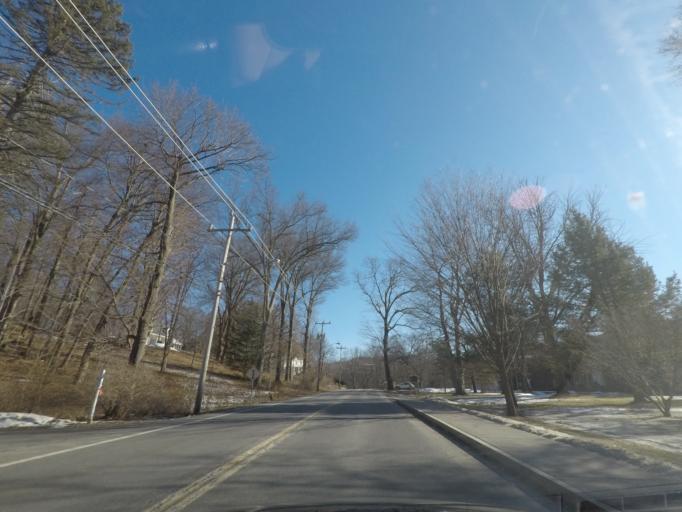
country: US
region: New York
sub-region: Columbia County
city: Chatham
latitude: 42.3552
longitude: -73.5984
